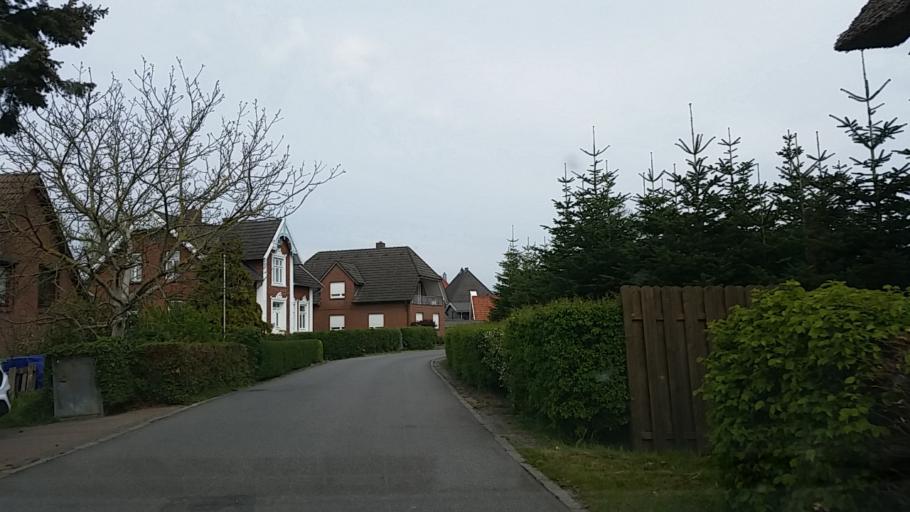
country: DE
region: Hamburg
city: Rothenburgsort
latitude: 53.4788
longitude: 10.0883
